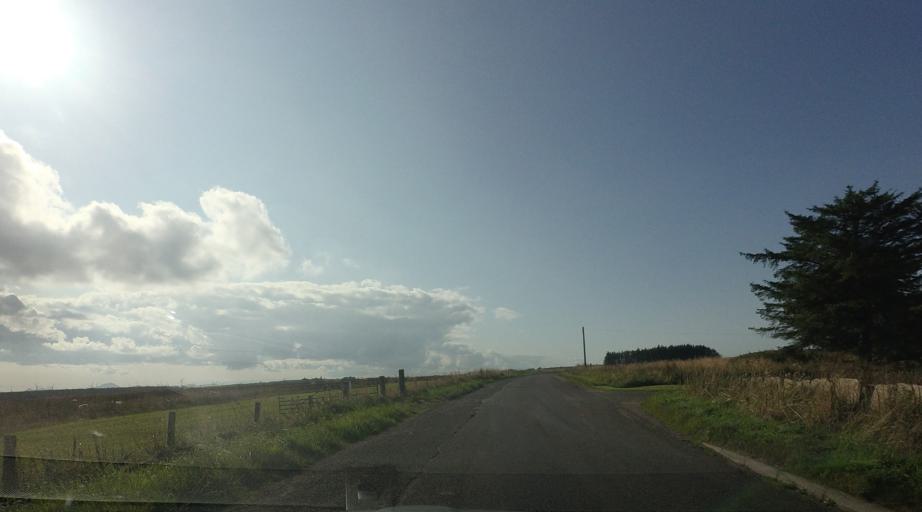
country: GB
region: Scotland
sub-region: Highland
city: Thurso
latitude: 58.4708
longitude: -3.3886
